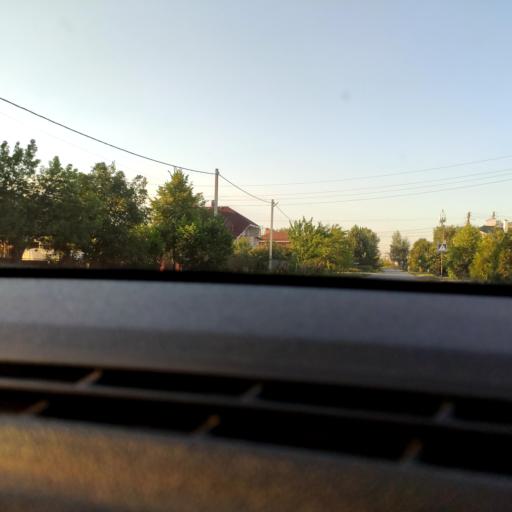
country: RU
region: Samara
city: Podstepki
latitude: 53.5769
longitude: 49.0672
